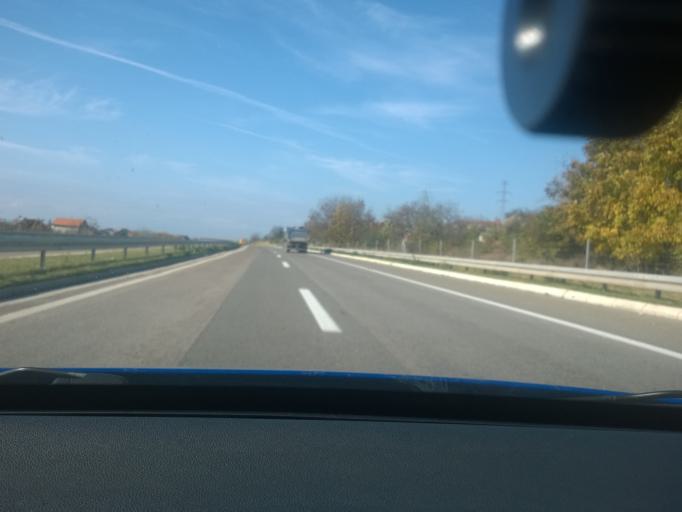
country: RS
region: Central Serbia
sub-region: Nisavski Okrug
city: Nis
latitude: 43.3424
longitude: 21.9203
